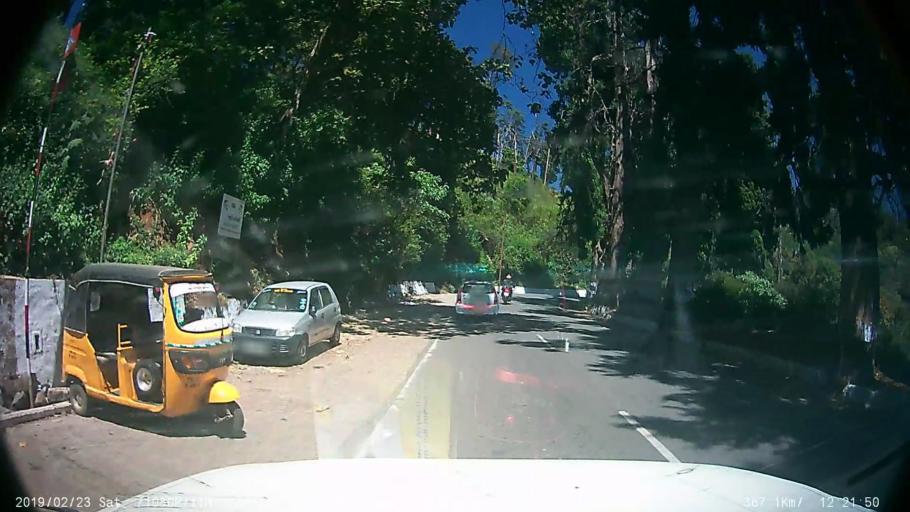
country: IN
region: Tamil Nadu
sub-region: Nilgiri
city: Wellington
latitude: 11.3372
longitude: 76.7984
